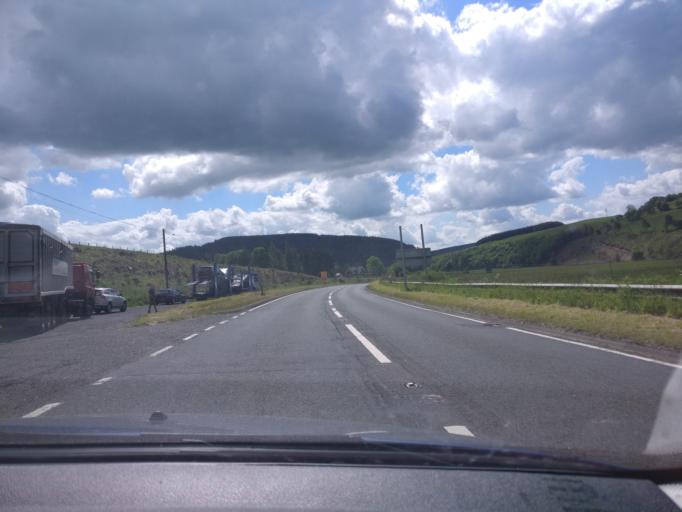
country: GB
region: Scotland
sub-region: Fife
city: Pathhead
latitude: 55.7595
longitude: -2.9253
